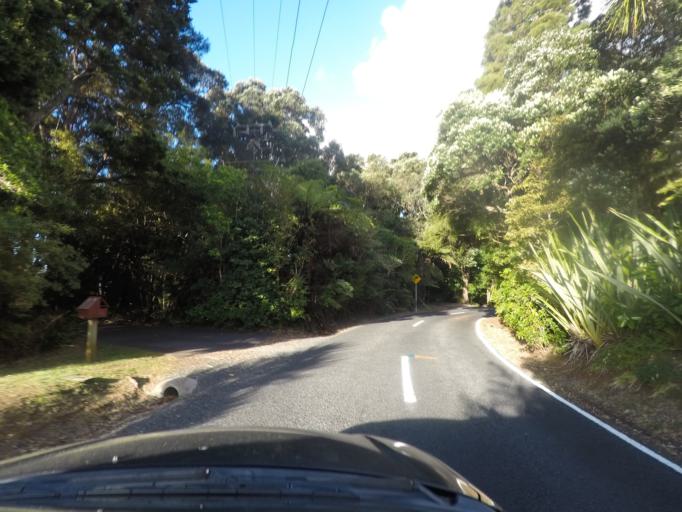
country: NZ
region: Auckland
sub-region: Auckland
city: Titirangi
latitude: -36.9370
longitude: 174.6239
